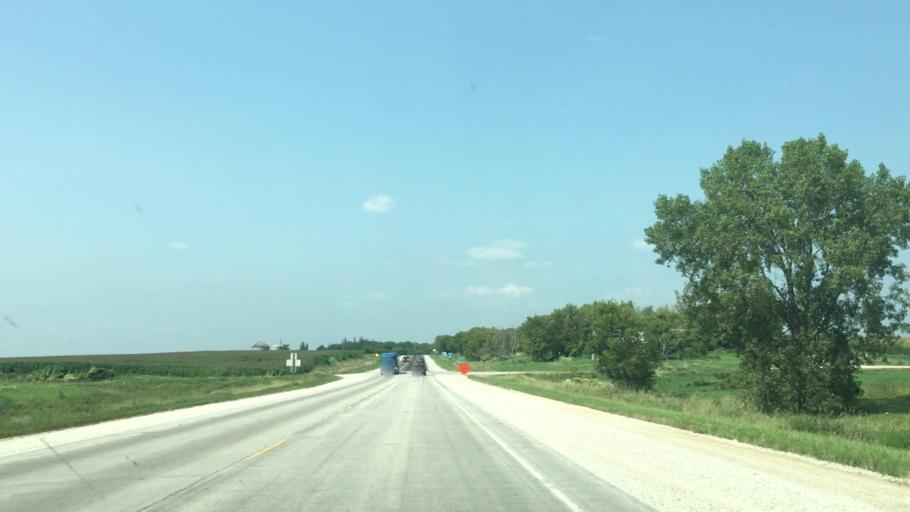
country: US
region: Minnesota
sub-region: Fillmore County
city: Harmony
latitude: 43.4995
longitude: -91.8711
